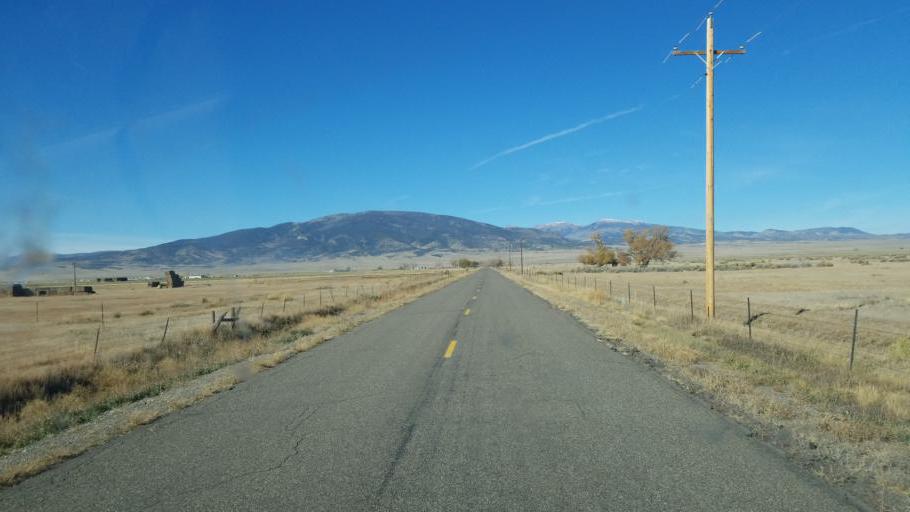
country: US
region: Colorado
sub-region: Rio Grande County
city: Monte Vista
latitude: 37.4591
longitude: -106.1187
